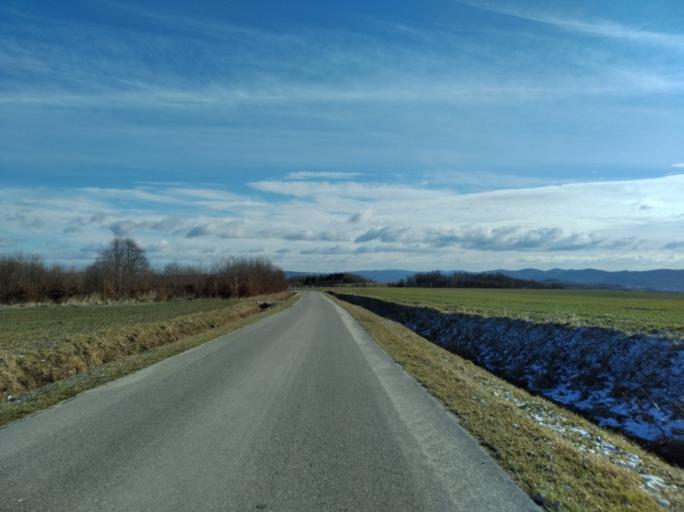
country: PL
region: Subcarpathian Voivodeship
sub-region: Powiat strzyzowski
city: Wisniowa
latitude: 49.9090
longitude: 21.6429
